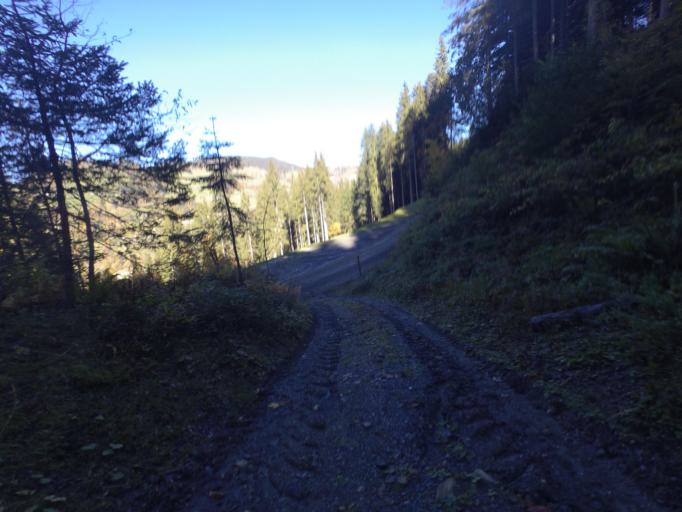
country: AT
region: Salzburg
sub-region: Politischer Bezirk Sankt Johann im Pongau
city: Sankt Johann im Pongau
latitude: 47.3251
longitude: 13.2316
